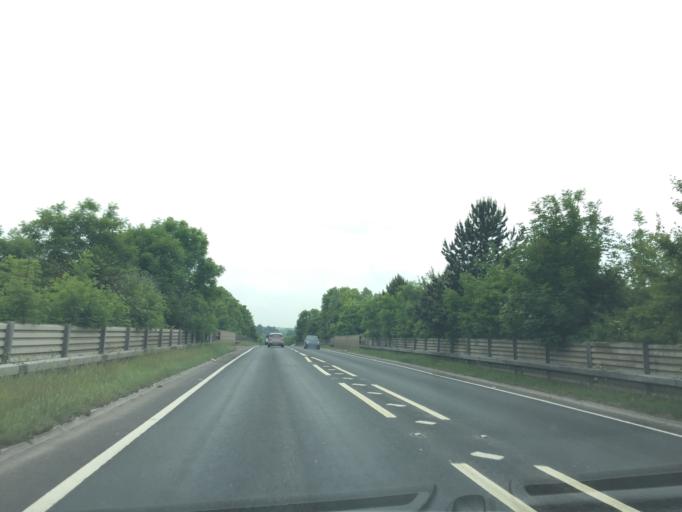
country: GB
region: England
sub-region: Dorset
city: Dorchester
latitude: 50.7094
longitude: -2.4199
